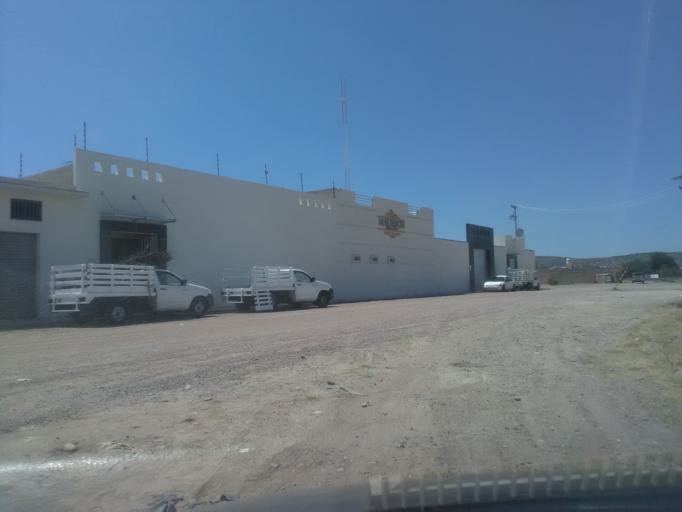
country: MX
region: Durango
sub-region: Durango
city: Sebastian Lerdo de Tejada
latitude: 23.9795
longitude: -104.6497
